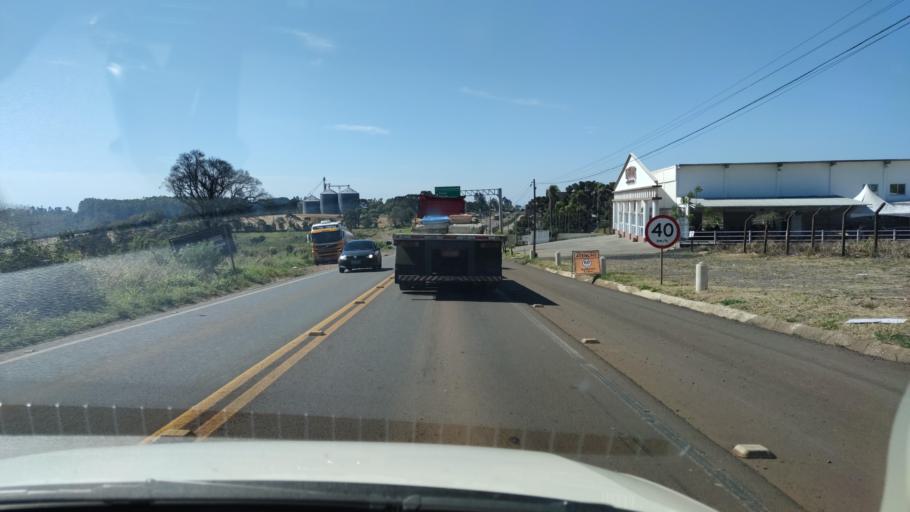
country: BR
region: Santa Catarina
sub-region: Sao Lourenco Do Oeste
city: Sao Lourenco dOeste
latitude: -26.3489
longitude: -52.8551
